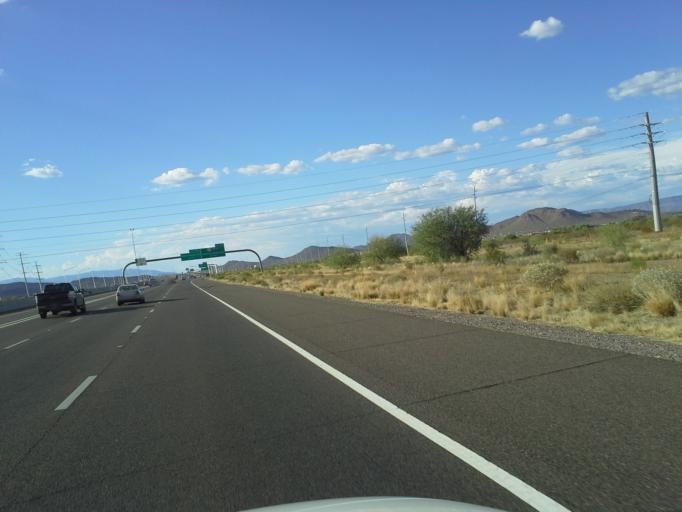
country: US
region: Arizona
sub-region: Maricopa County
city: Anthem
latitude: 33.7574
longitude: -112.1266
